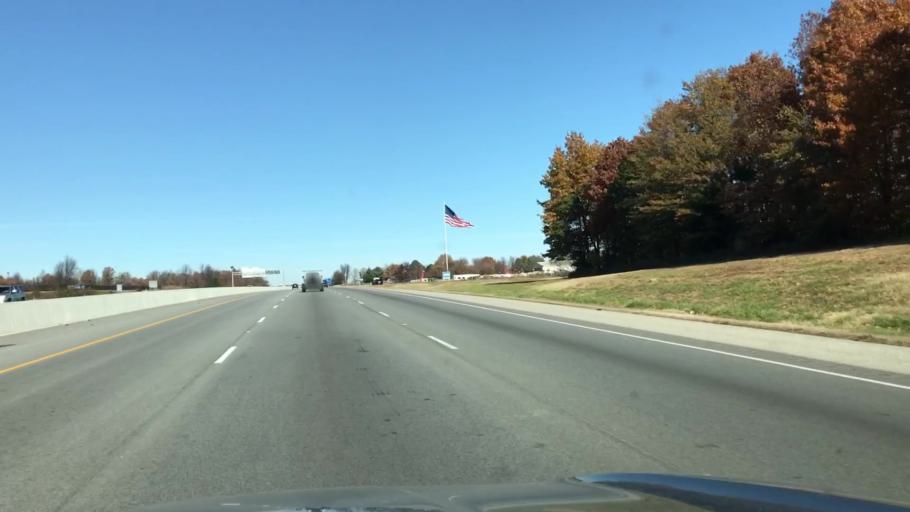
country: US
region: Arkansas
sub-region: Benton County
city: Lowell
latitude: 36.2562
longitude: -94.1499
